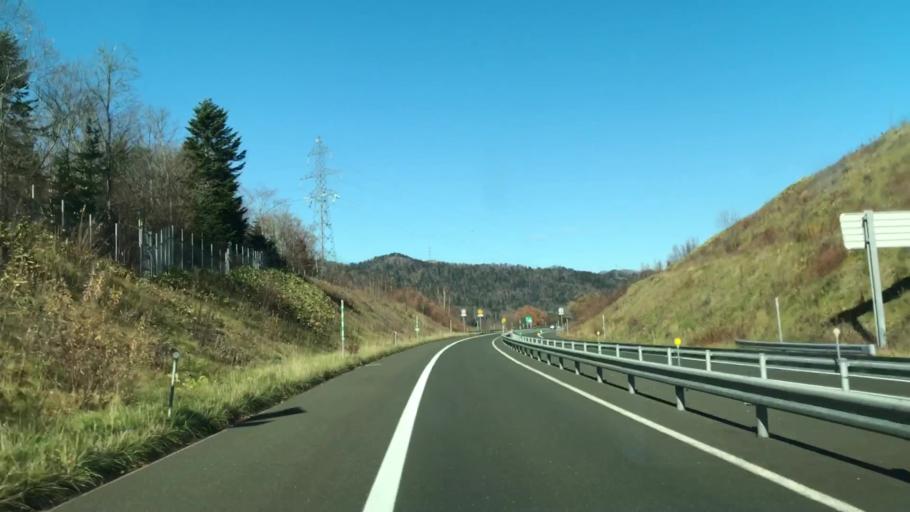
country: JP
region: Hokkaido
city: Shimo-furano
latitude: 42.9993
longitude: 142.4102
